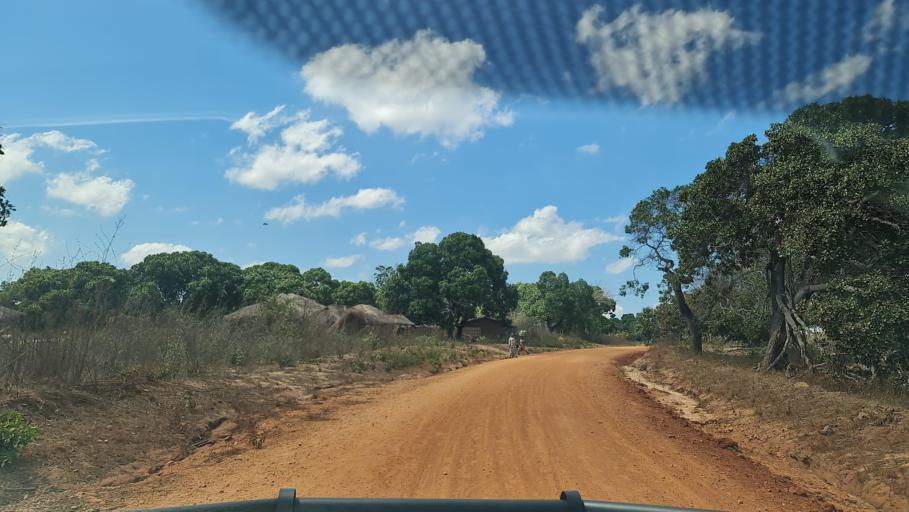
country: MZ
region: Nampula
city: Nacala
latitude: -14.1697
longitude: 40.2571
